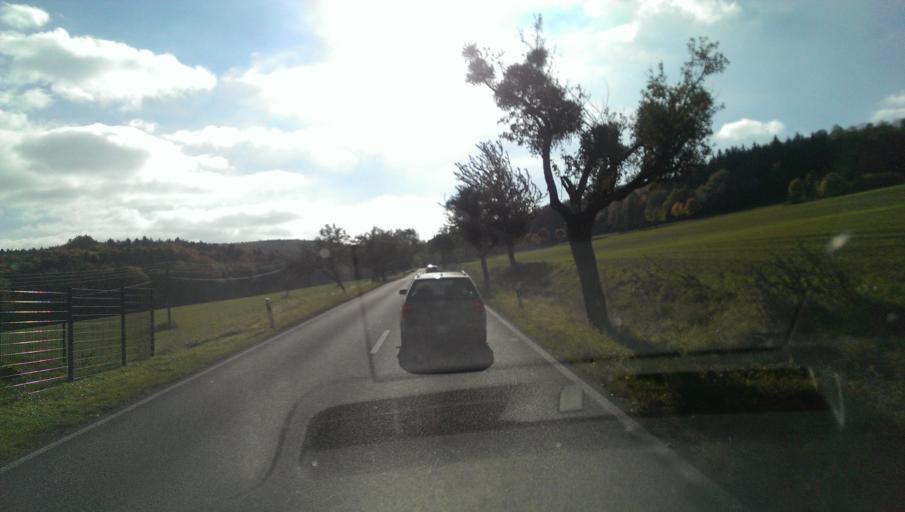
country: DE
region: Saxony
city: Dohma
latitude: 50.8693
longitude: 13.9554
